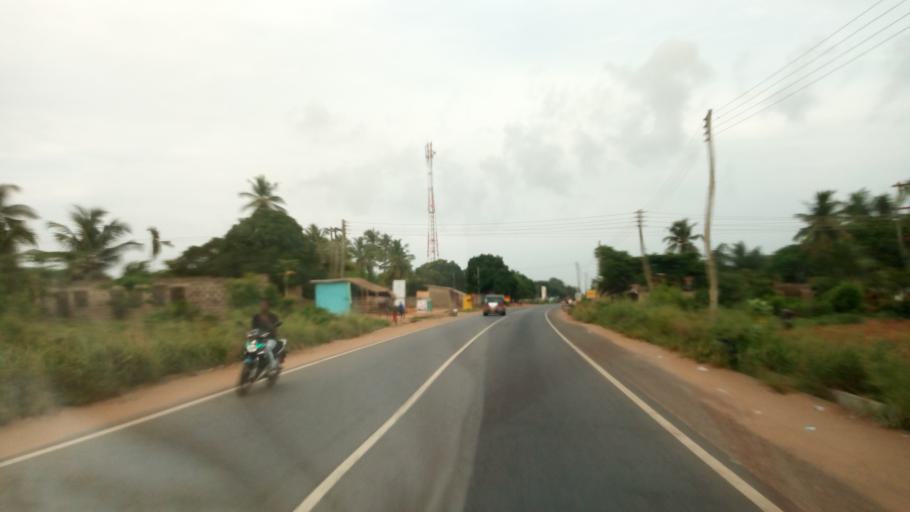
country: TG
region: Maritime
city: Lome
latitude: 6.0813
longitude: 1.0520
